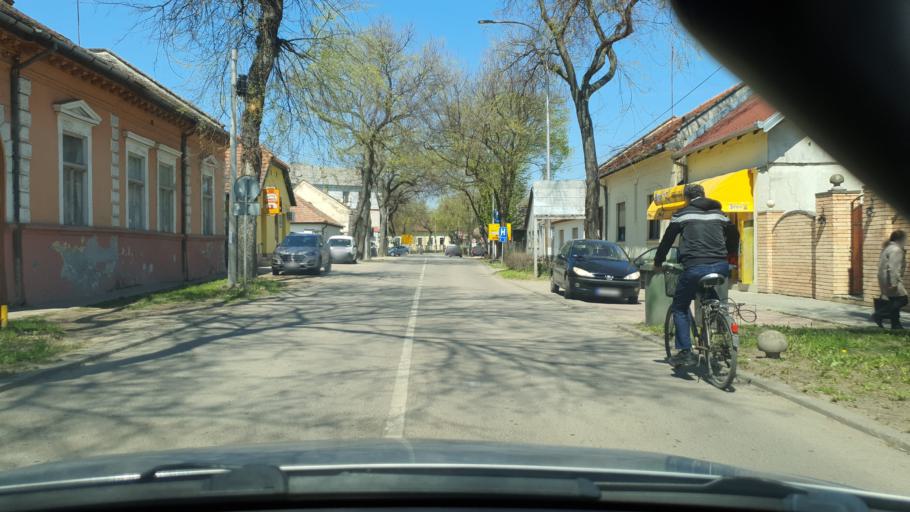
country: RS
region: Autonomna Pokrajina Vojvodina
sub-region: Zapadnobacki Okrug
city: Sombor
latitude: 45.7667
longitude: 19.1083
